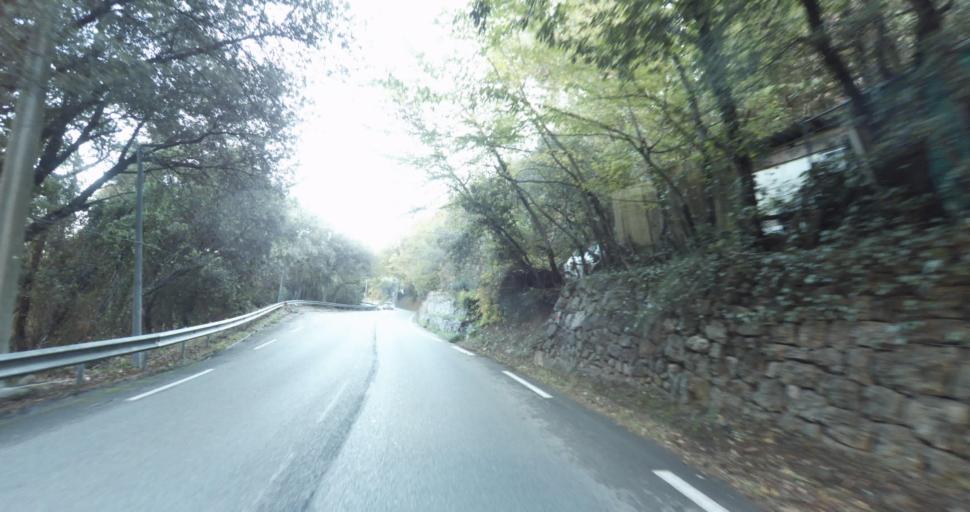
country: FR
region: Provence-Alpes-Cote d'Azur
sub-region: Departement des Alpes-Maritimes
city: Saint-Jeannet
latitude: 43.7454
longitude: 7.1307
